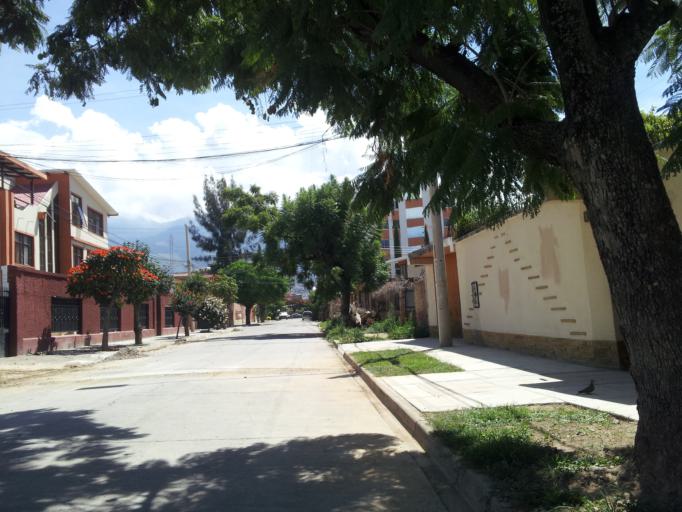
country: BO
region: Cochabamba
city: Cochabamba
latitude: -17.3843
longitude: -66.1725
